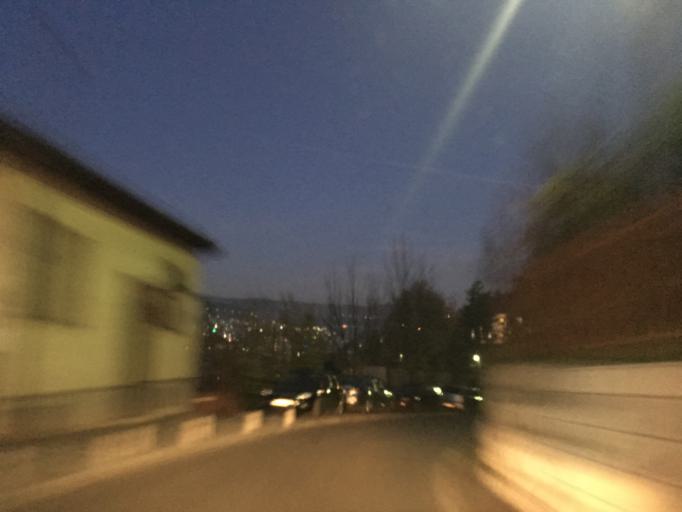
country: BA
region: Federation of Bosnia and Herzegovina
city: Kobilja Glava
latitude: 43.8532
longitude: 18.4163
